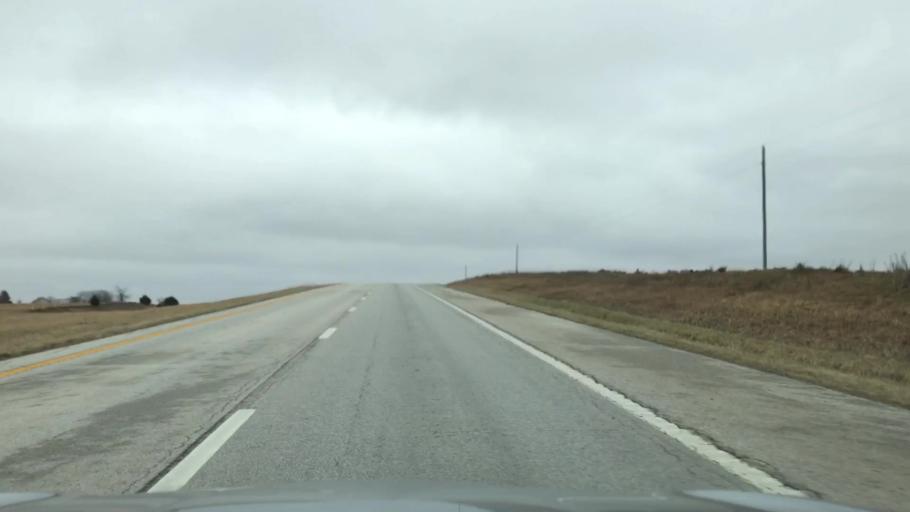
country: US
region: Missouri
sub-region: Linn County
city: Marceline
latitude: 39.7601
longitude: -92.9206
